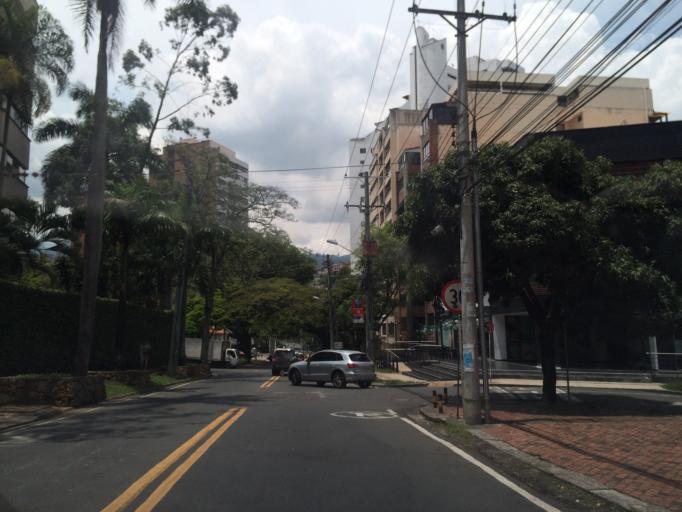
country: CO
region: Valle del Cauca
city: Cali
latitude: 3.4516
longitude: -76.5475
